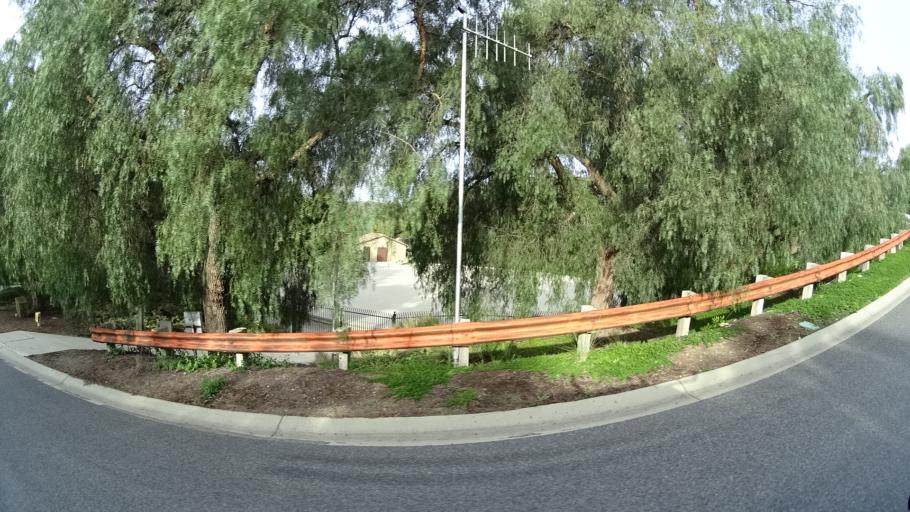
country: US
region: California
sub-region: Ventura County
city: Thousand Oaks
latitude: 34.1876
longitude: -118.8127
